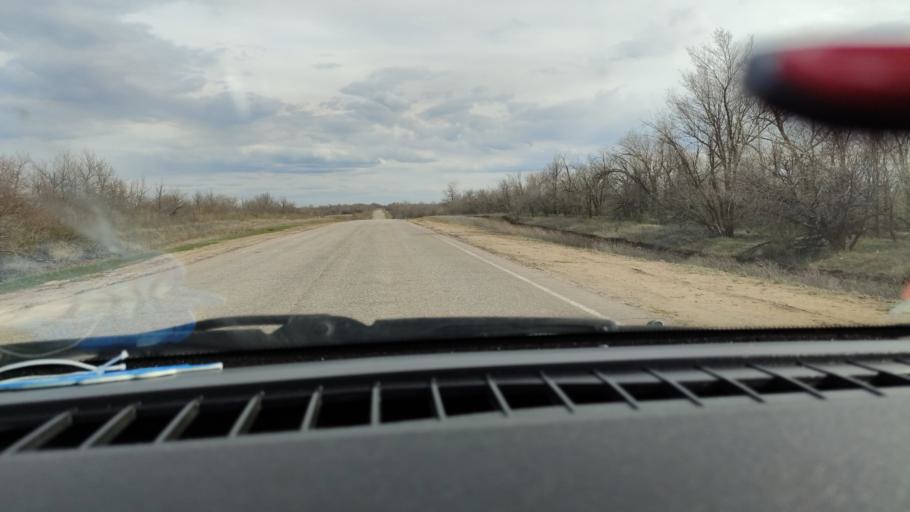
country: RU
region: Saratov
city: Rovnoye
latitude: 50.9893
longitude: 46.1107
